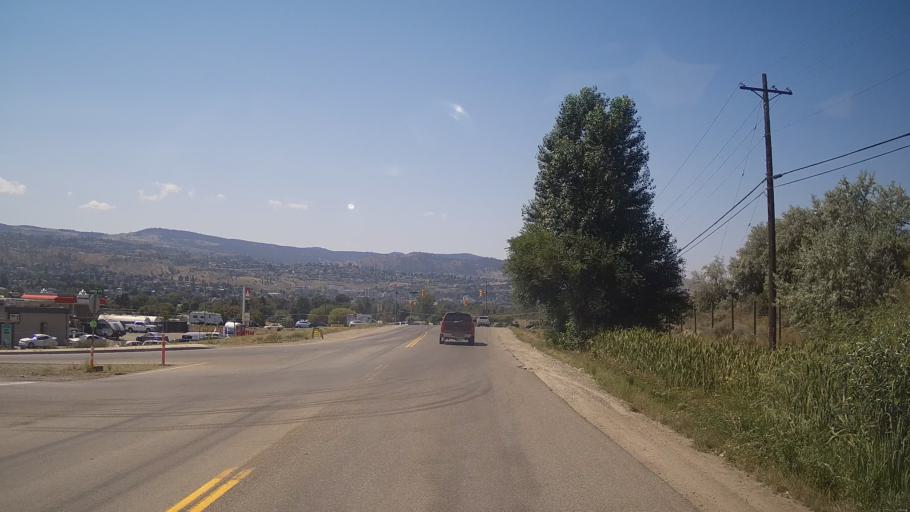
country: CA
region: British Columbia
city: Kamloops
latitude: 50.6827
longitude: -120.2965
